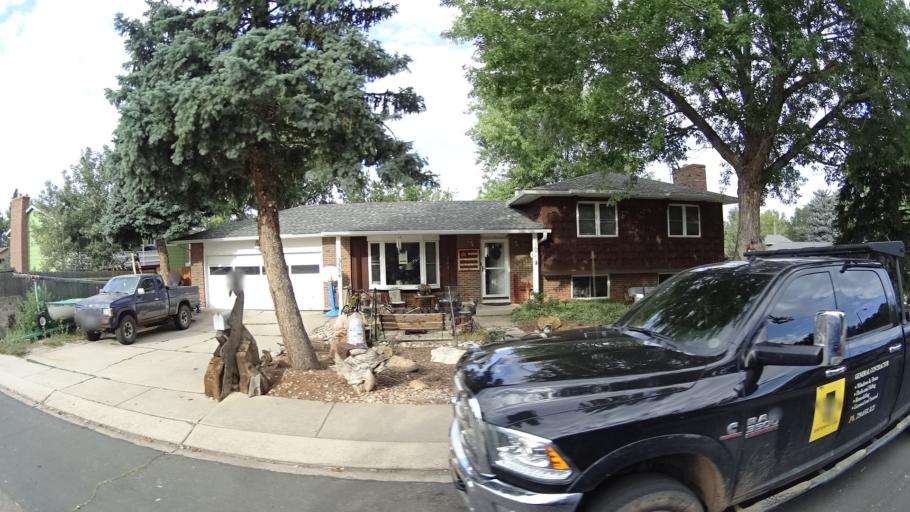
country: US
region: Colorado
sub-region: El Paso County
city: Cimarron Hills
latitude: 38.8660
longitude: -104.7521
